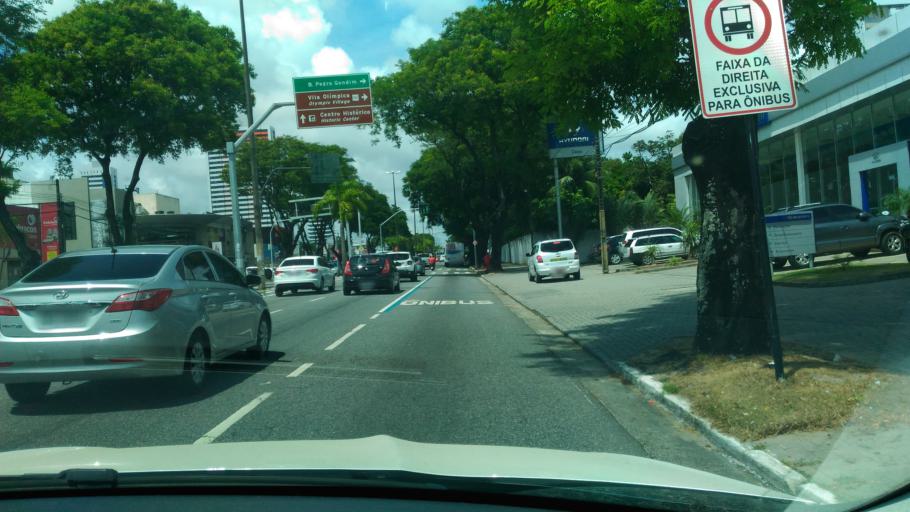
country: BR
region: Paraiba
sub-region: Joao Pessoa
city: Joao Pessoa
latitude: -7.1196
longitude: -34.8463
